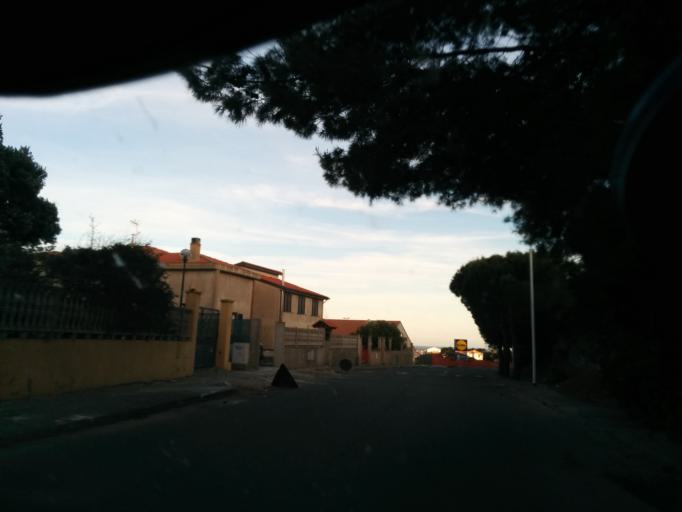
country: IT
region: Sardinia
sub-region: Provincia di Carbonia-Iglesias
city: Sant'Antioco
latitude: 39.0591
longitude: 8.4480
